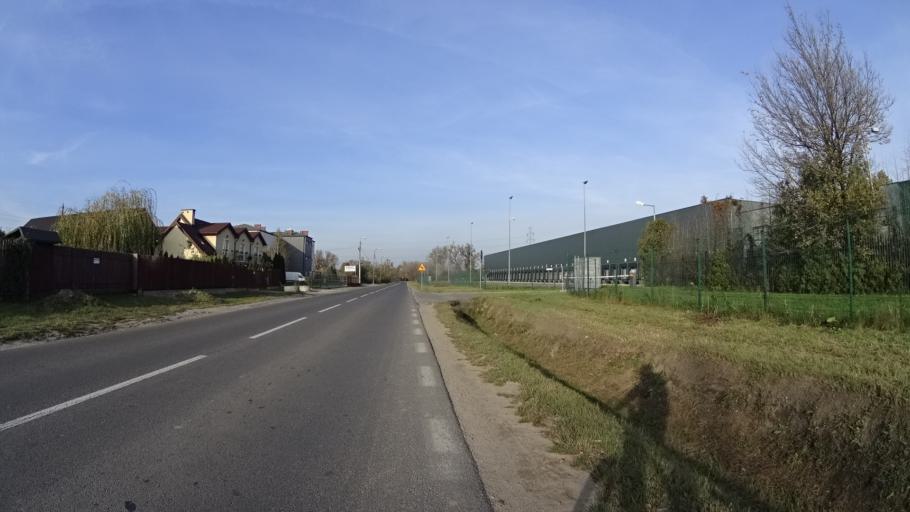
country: PL
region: Masovian Voivodeship
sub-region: Powiat warszawski zachodni
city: Babice
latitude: 52.2824
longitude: 20.8671
